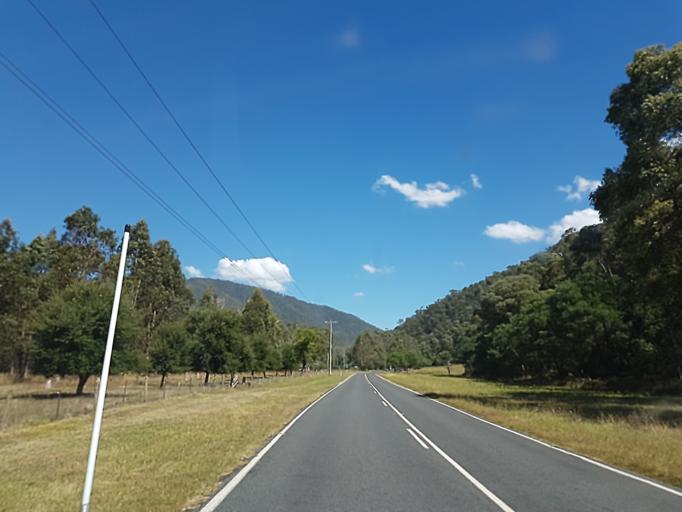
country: AU
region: Victoria
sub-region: Alpine
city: Mount Beauty
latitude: -36.8405
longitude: 147.0785
